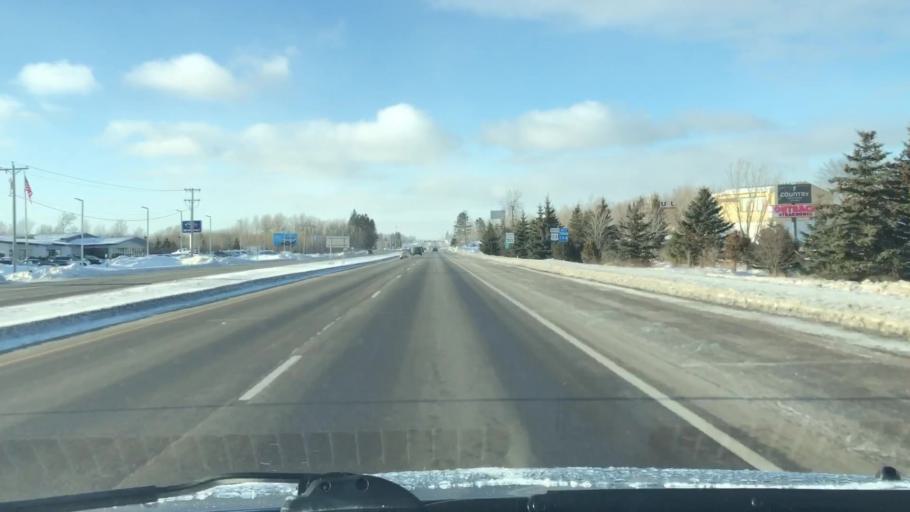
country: US
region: Minnesota
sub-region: Saint Louis County
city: Hermantown
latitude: 46.8155
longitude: -92.1757
